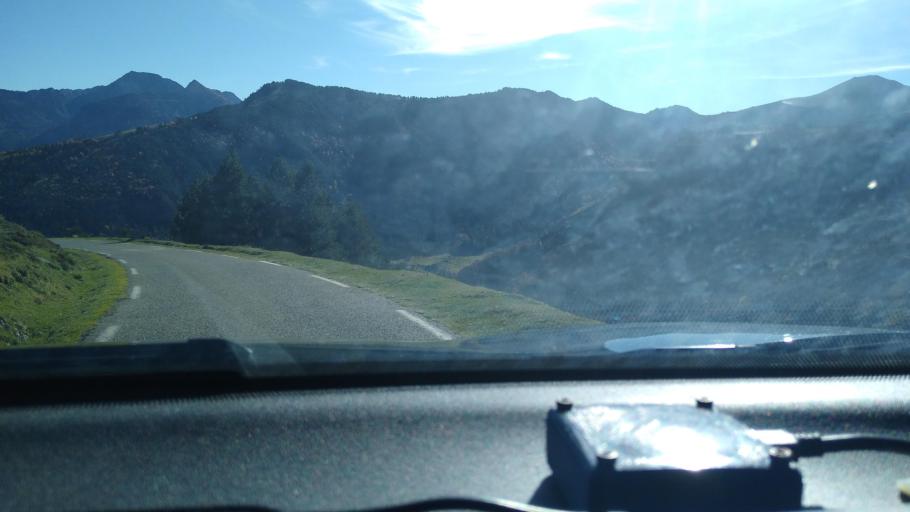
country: FR
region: Midi-Pyrenees
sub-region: Departement de l'Ariege
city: Ax-les-Thermes
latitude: 42.7342
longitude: 2.0027
